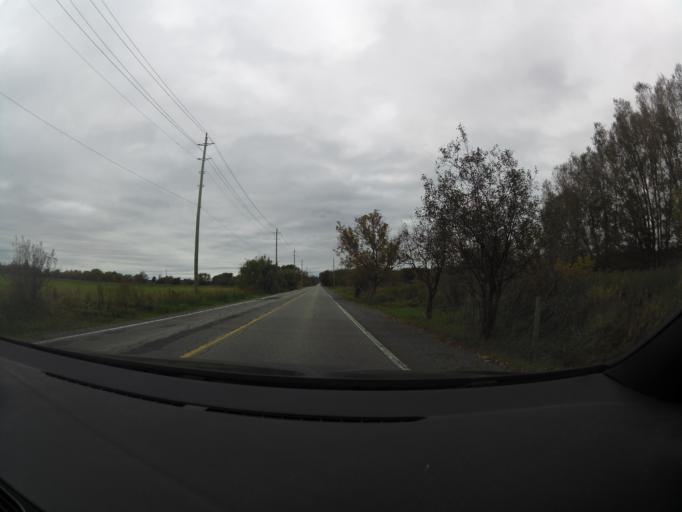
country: CA
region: Ontario
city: Bells Corners
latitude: 45.3199
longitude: -75.9591
